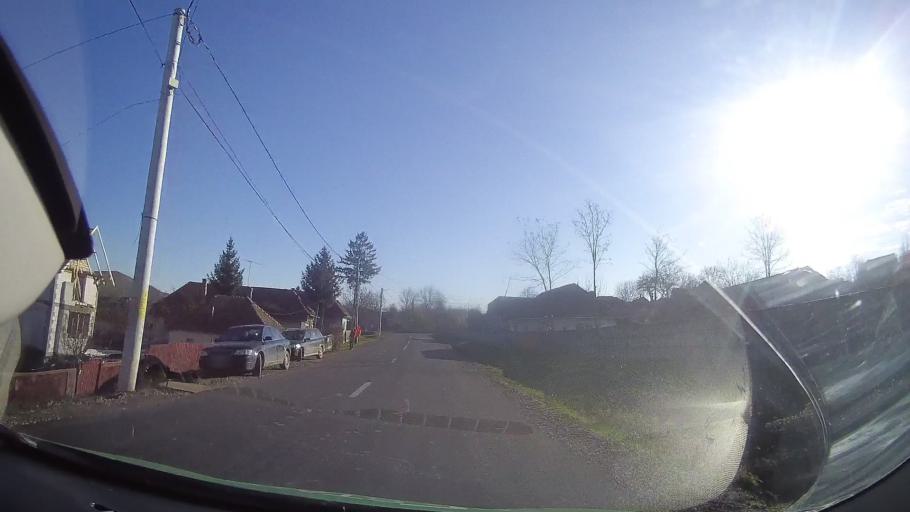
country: RO
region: Mures
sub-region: Comuna Band
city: Band
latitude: 46.5807
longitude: 24.3632
